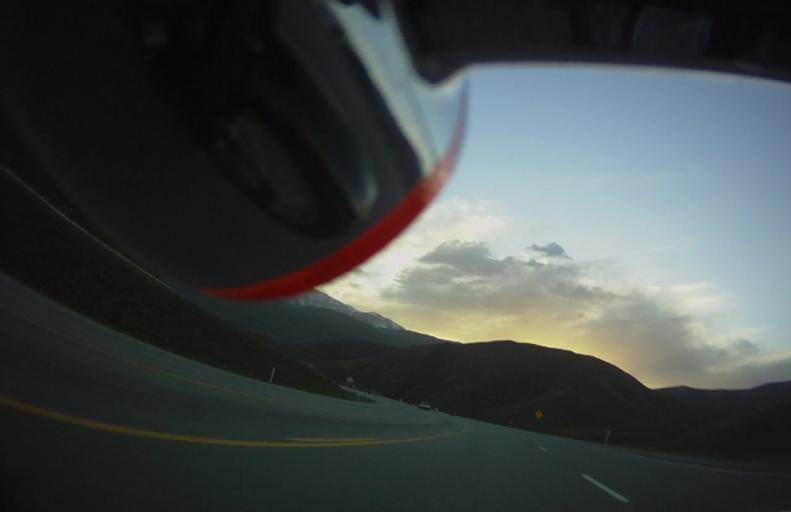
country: US
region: Utah
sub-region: Wasatch County
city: Midway
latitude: 40.4110
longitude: -111.5090
